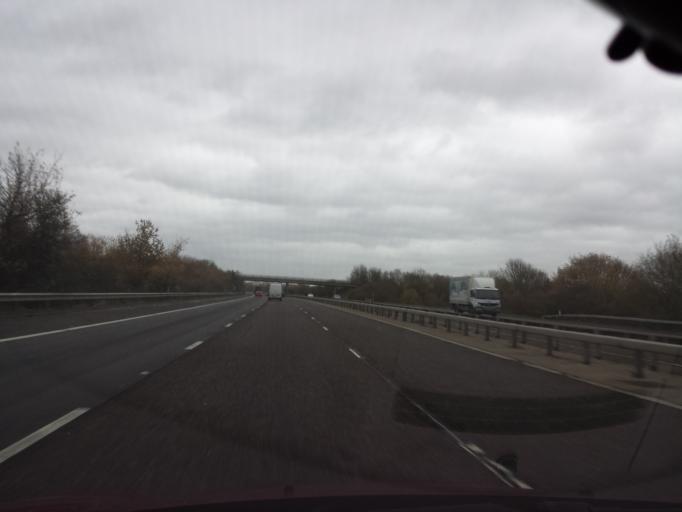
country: GB
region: England
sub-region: Surrey
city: Shepperton
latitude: 51.3940
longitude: -0.4688
